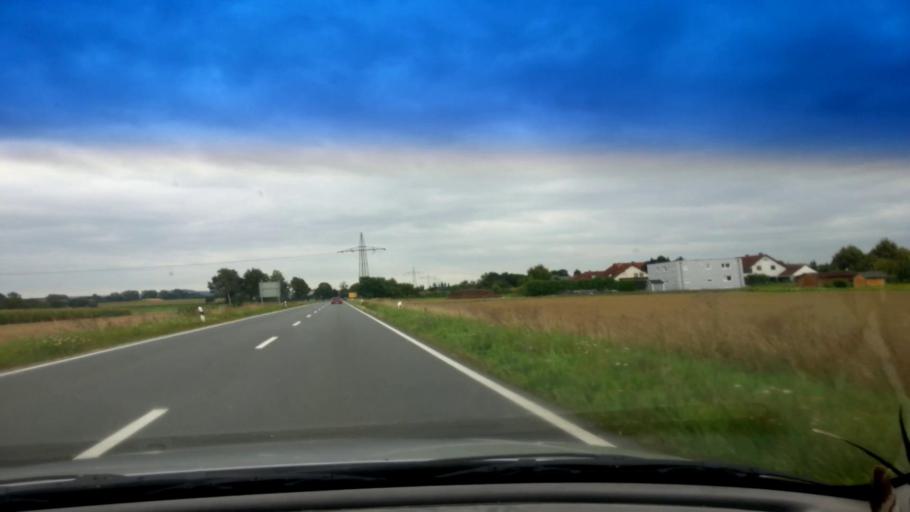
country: DE
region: Bavaria
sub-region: Upper Franconia
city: Hirschaid
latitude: 49.8282
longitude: 10.9916
